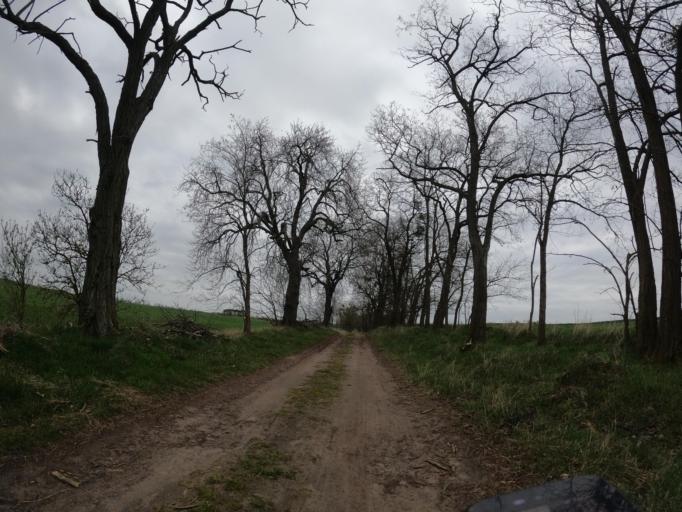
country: DE
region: Brandenburg
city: Werftpfuhl
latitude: 52.5905
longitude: 13.7980
